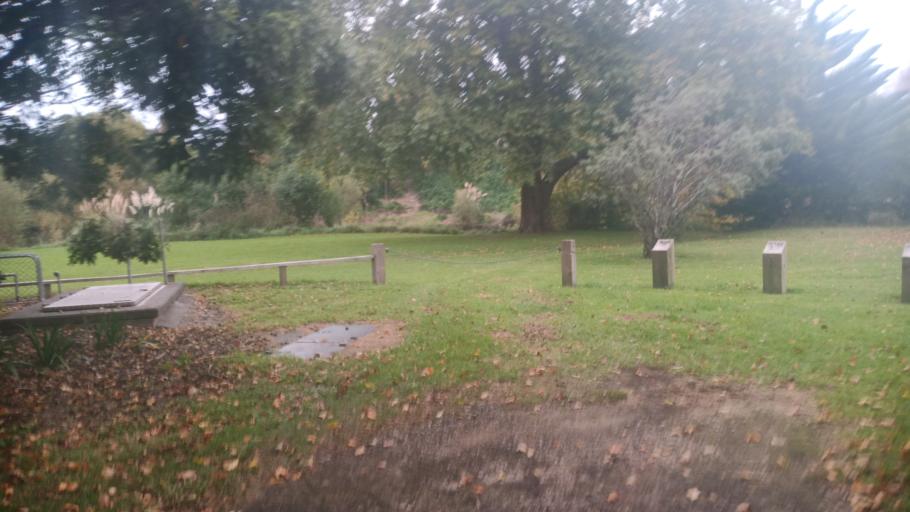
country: NZ
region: Gisborne
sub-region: Gisborne District
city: Gisborne
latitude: -38.6660
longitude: 178.0397
